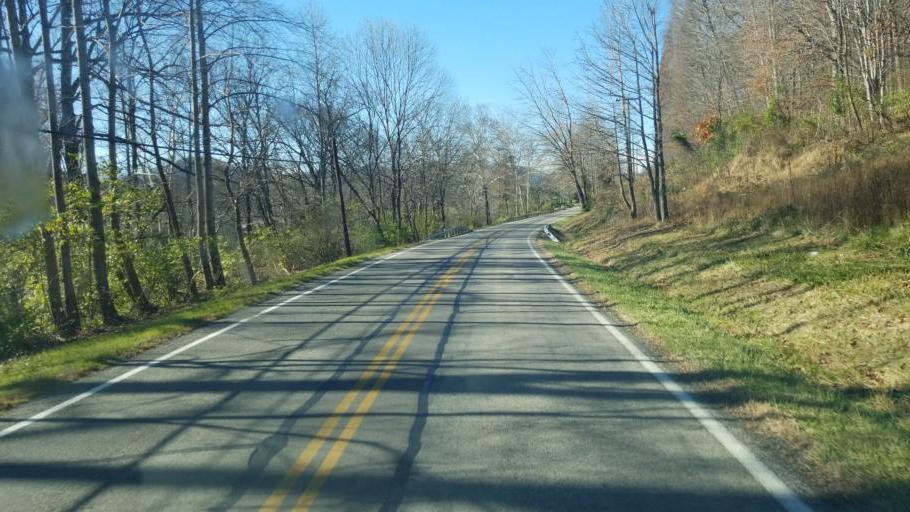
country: US
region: Kentucky
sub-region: Lewis County
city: Vanceburg
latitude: 38.6220
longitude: -83.1824
